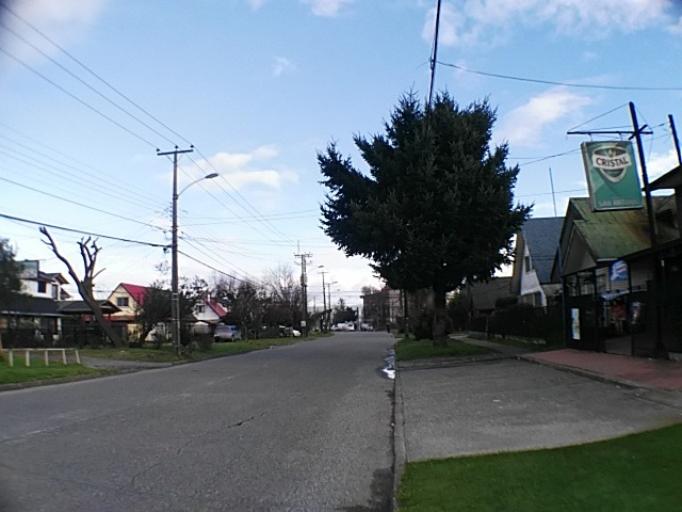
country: CL
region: Los Lagos
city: Las Animas
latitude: -39.8351
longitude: -73.2227
